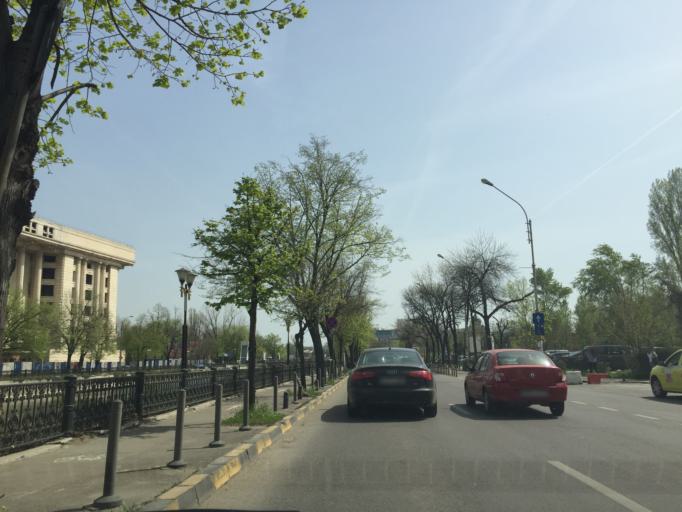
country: RO
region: Bucuresti
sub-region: Municipiul Bucuresti
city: Bucuresti
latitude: 44.4368
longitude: 26.0725
